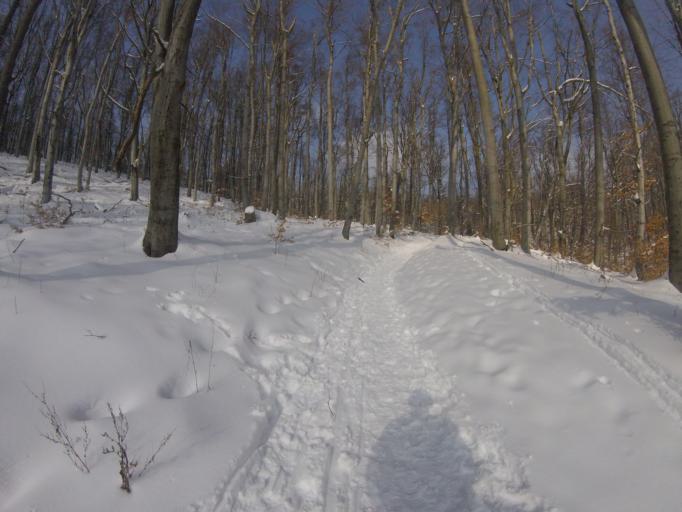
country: HU
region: Pest
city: Pilisszentkereszt
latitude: 47.7144
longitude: 18.8902
